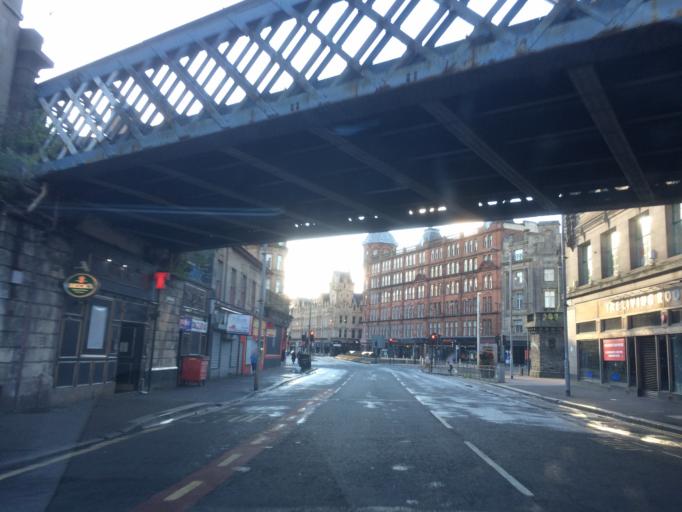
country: GB
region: Scotland
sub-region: Glasgow City
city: Glasgow
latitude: 55.8560
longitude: -4.2429
